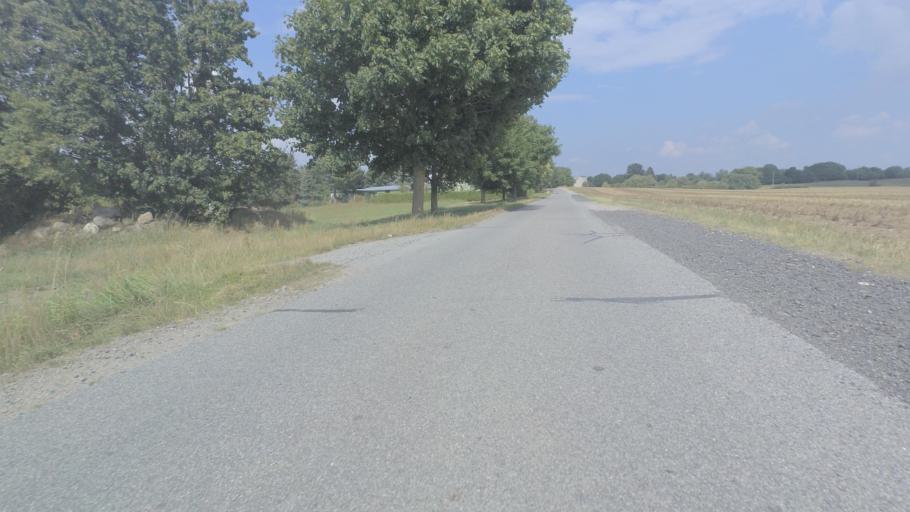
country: DE
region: Mecklenburg-Vorpommern
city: Borrentin
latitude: 53.8486
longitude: 12.9528
